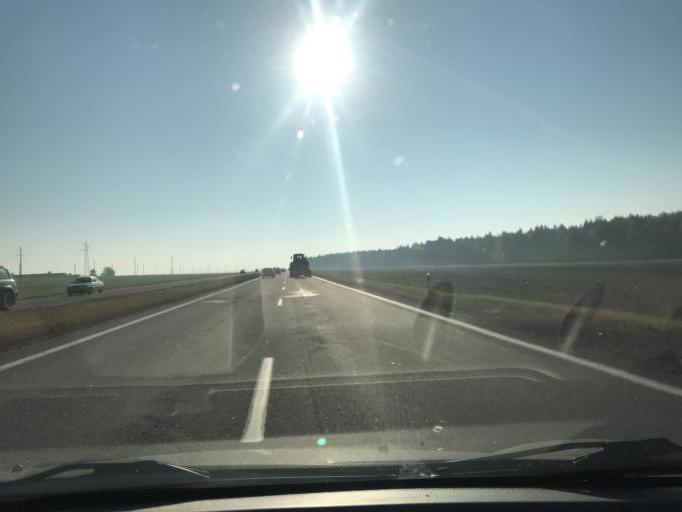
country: BY
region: Minsk
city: Dukora
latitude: 53.6156
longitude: 28.0572
